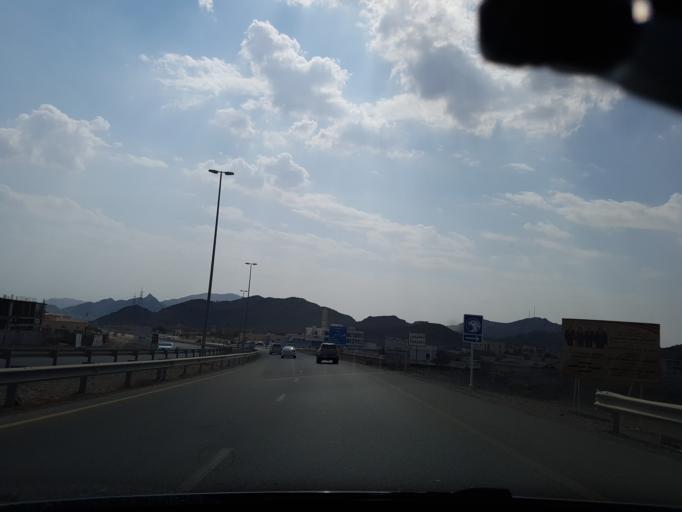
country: AE
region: Al Fujayrah
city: Dibba Al-Fujairah
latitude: 25.5131
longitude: 56.0759
